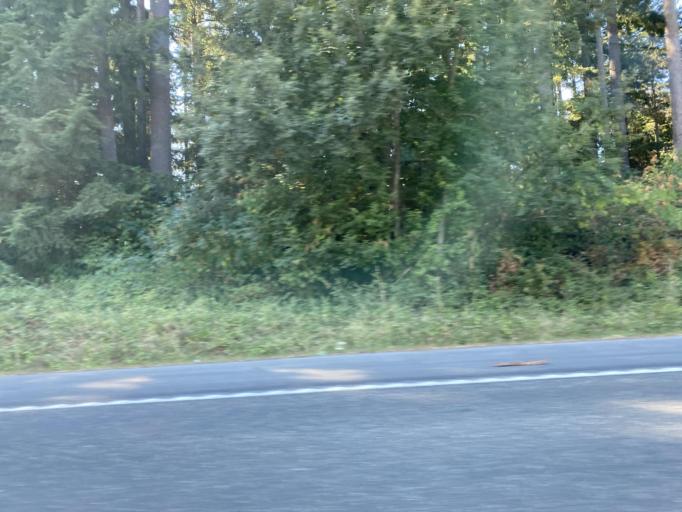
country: US
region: Washington
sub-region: Thurston County
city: Tanglewilde-Thompson Place
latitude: 46.9863
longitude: -122.7543
